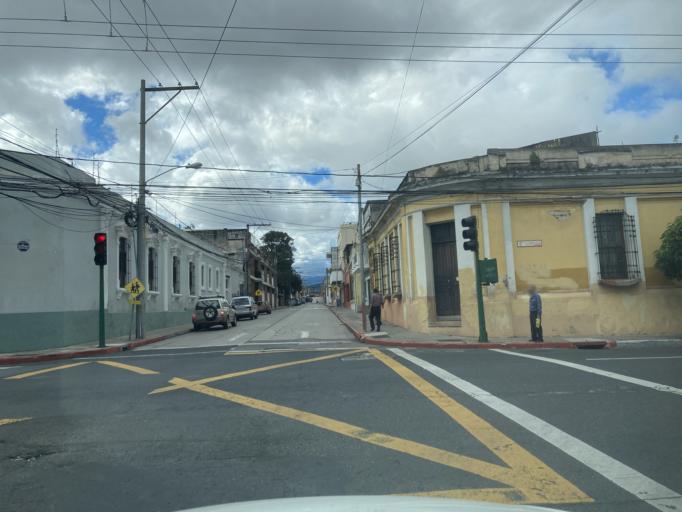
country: GT
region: Guatemala
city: Guatemala City
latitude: 14.6466
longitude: -90.5117
